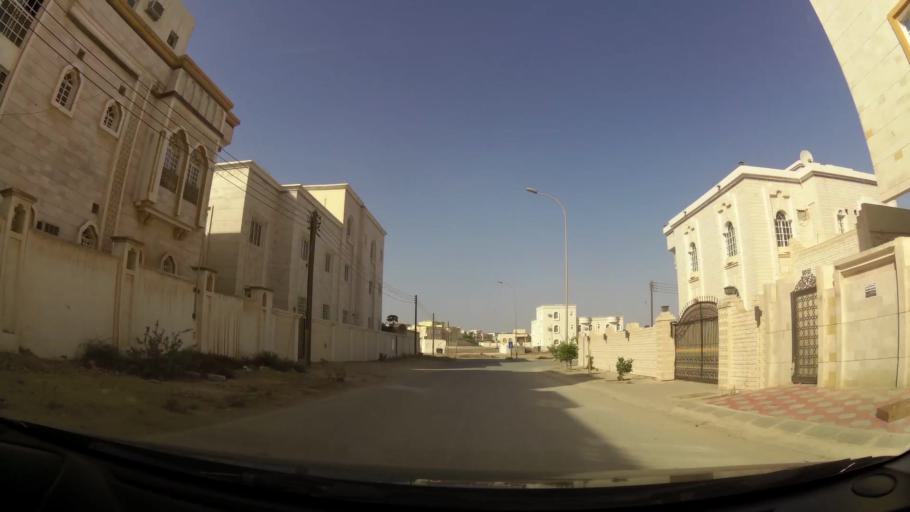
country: OM
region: Zufar
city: Salalah
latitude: 17.0090
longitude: 54.0246
